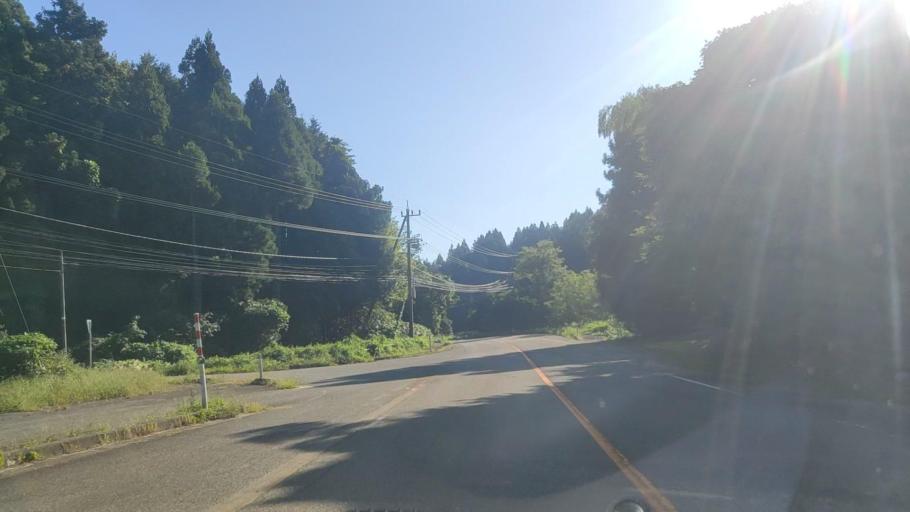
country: JP
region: Ishikawa
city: Nanao
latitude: 37.1234
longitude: 136.8630
